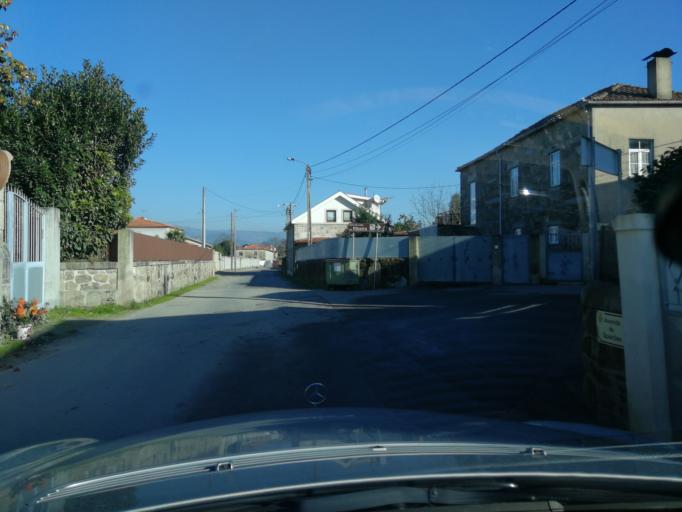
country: PT
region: Braga
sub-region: Braga
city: Adaufe
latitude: 41.6162
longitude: -8.4025
